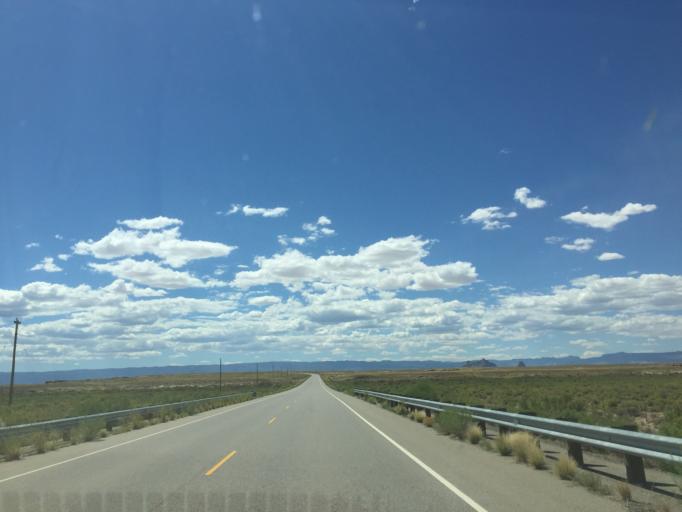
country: US
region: New Mexico
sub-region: San Juan County
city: Waterflow
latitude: 36.3678
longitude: -108.5685
